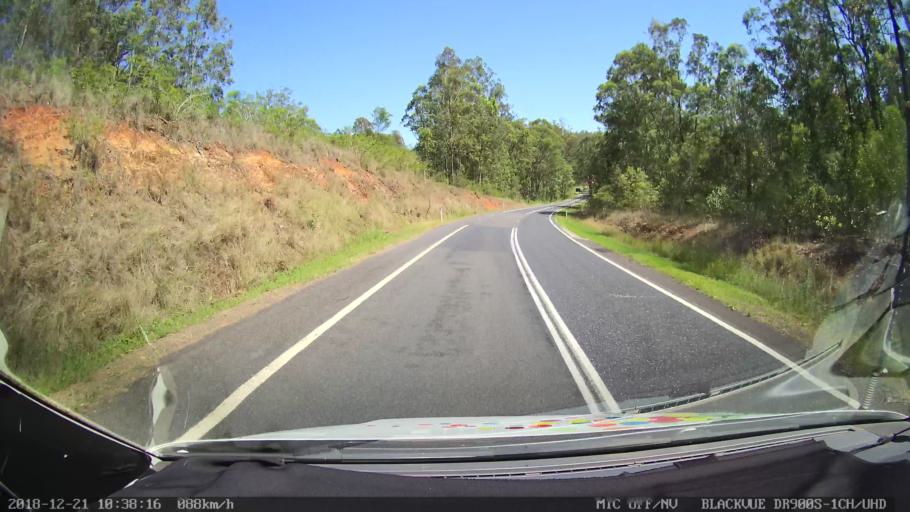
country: AU
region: New South Wales
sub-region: Clarence Valley
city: South Grafton
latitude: -29.6179
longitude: 152.6092
